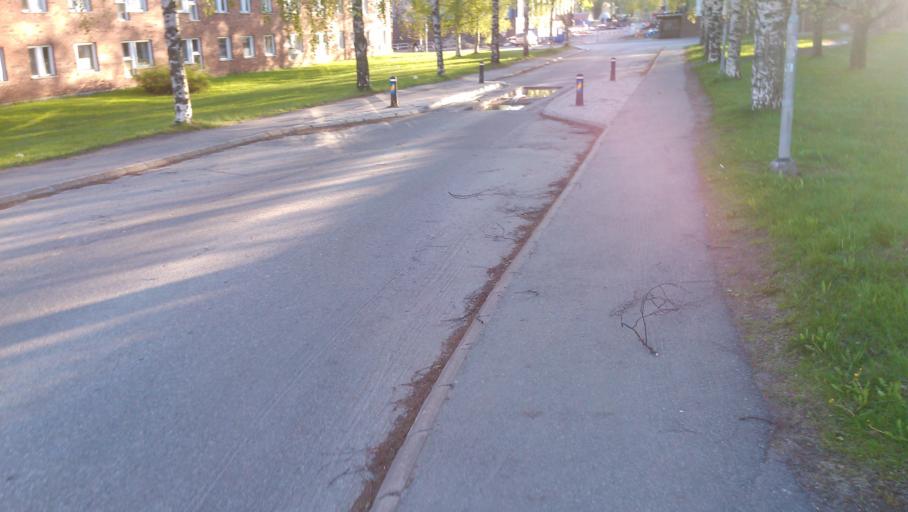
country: SE
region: Vaesterbotten
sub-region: Umea Kommun
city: Umea
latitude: 63.8109
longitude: 20.3180
